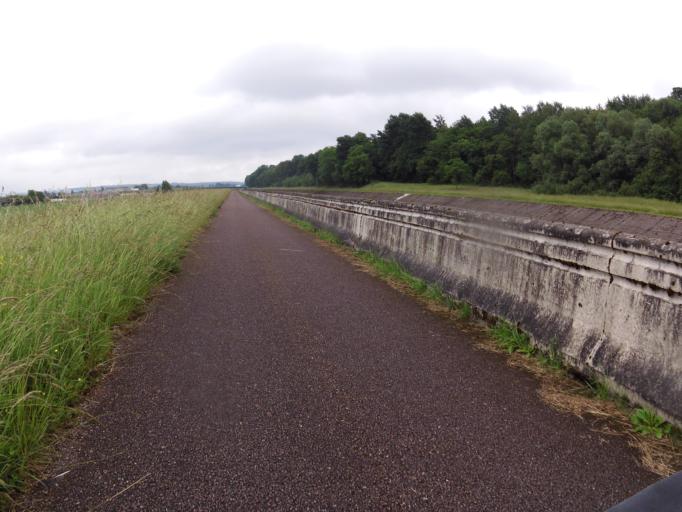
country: FR
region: Champagne-Ardenne
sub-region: Departement de la Haute-Marne
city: Saint-Dizier
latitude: 48.6198
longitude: 4.9278
